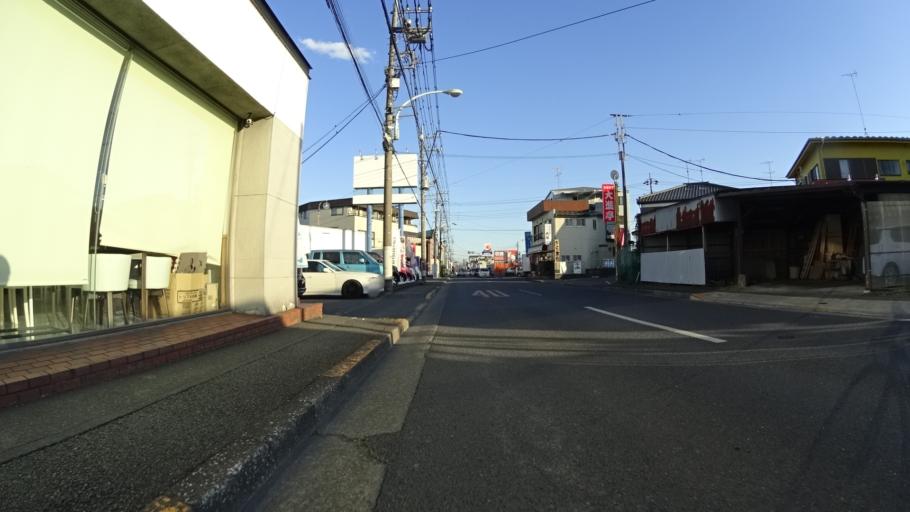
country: JP
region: Tokyo
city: Hachioji
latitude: 35.6785
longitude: 139.2838
